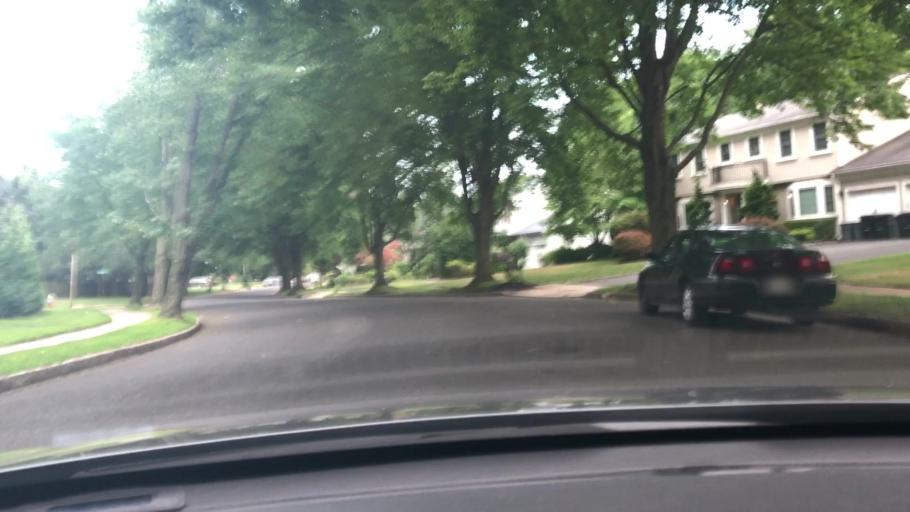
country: US
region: New Jersey
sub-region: Middlesex County
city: East Brunswick
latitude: 40.4217
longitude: -74.4281
